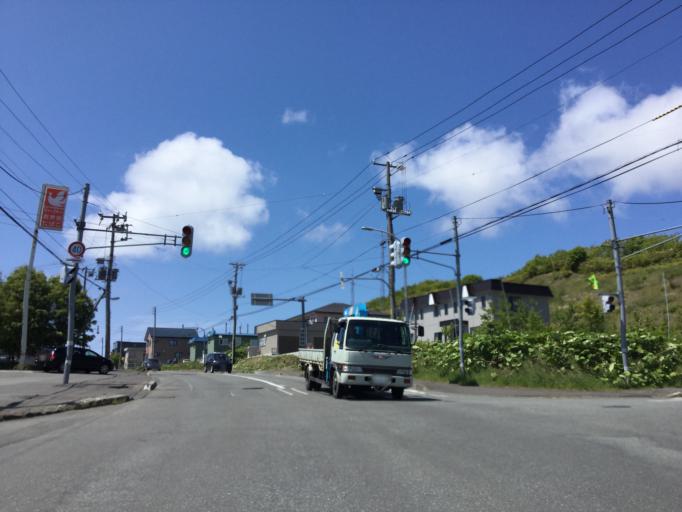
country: JP
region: Hokkaido
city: Wakkanai
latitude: 45.3865
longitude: 141.6864
